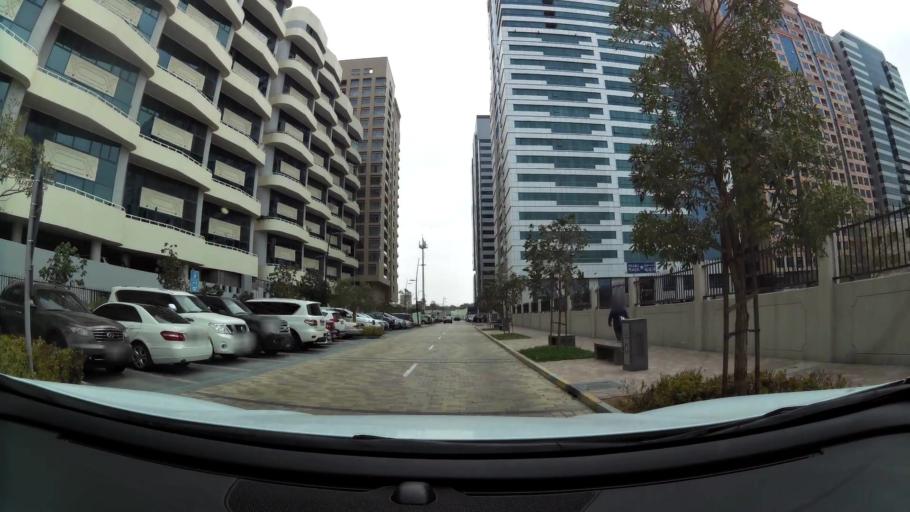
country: AE
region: Abu Dhabi
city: Abu Dhabi
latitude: 24.4700
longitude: 54.3396
